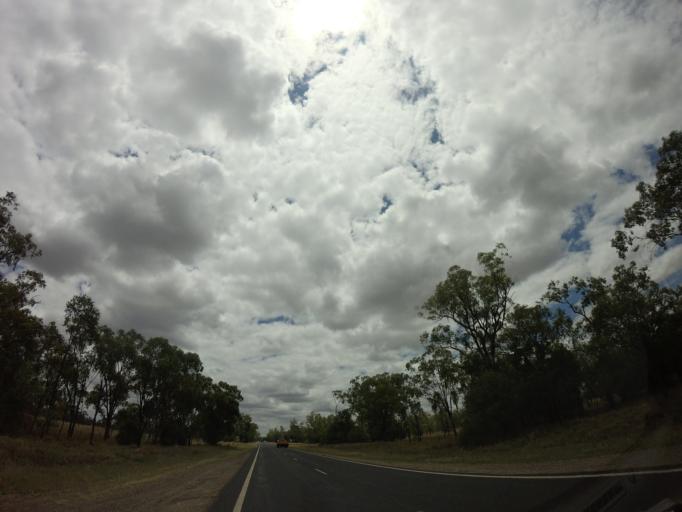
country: AU
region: Queensland
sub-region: Goondiwindi
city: Goondiwindi
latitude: -28.4886
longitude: 150.2928
